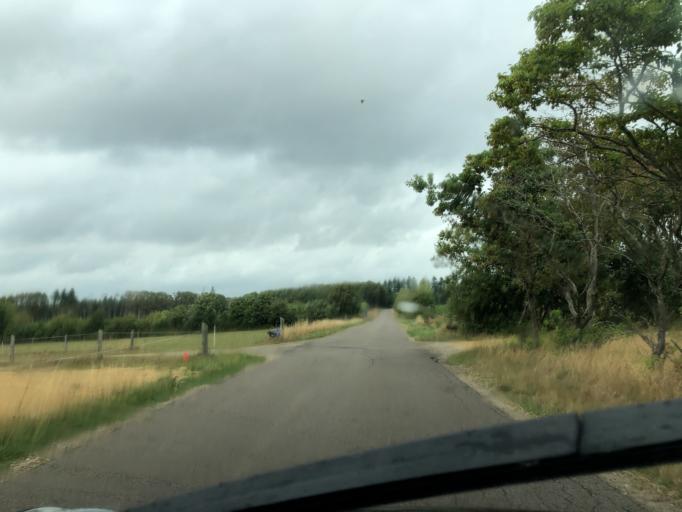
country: DK
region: Central Jutland
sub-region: Holstebro Kommune
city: Ulfborg
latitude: 56.1553
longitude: 8.4077
